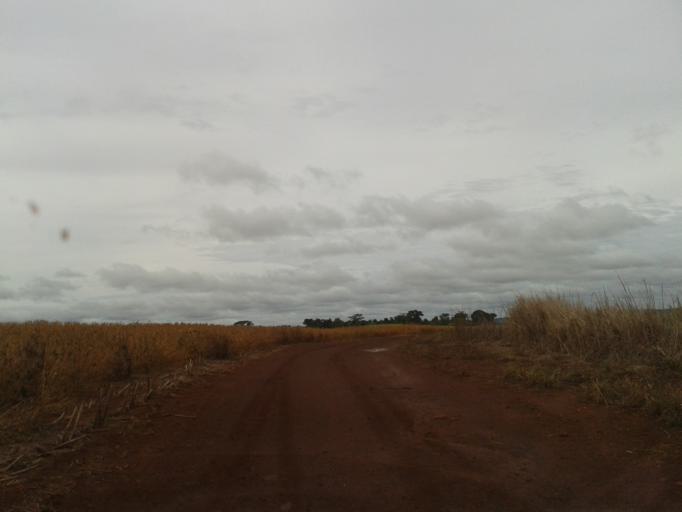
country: BR
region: Minas Gerais
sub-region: Capinopolis
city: Capinopolis
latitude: -18.7713
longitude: -49.7671
